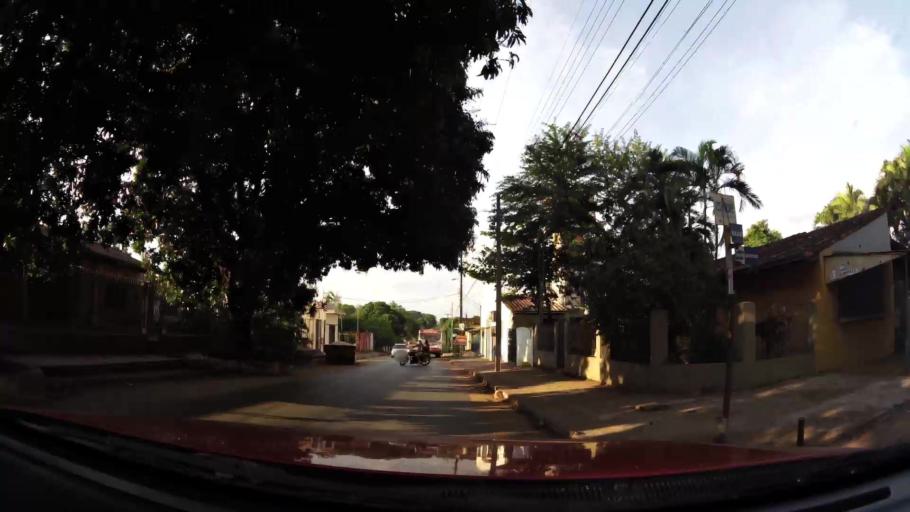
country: PY
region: Central
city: Nemby
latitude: -25.3682
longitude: -57.5311
